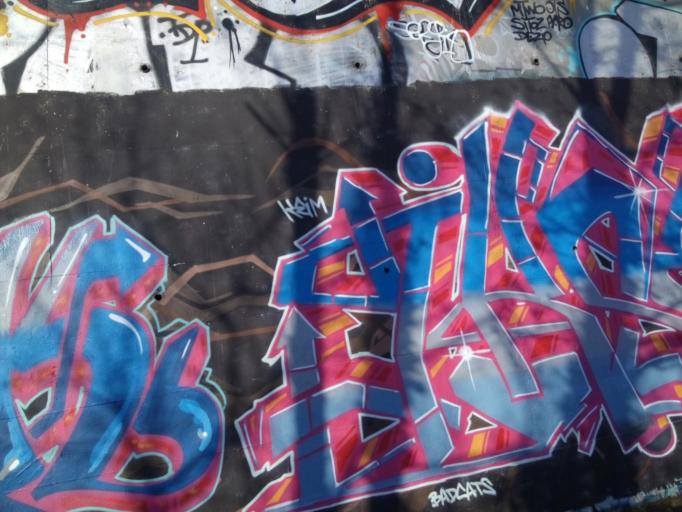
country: FR
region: Rhone-Alpes
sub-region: Departement de l'Isere
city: Saint-Martin-le-Vinoux
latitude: 45.2055
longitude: 5.7094
